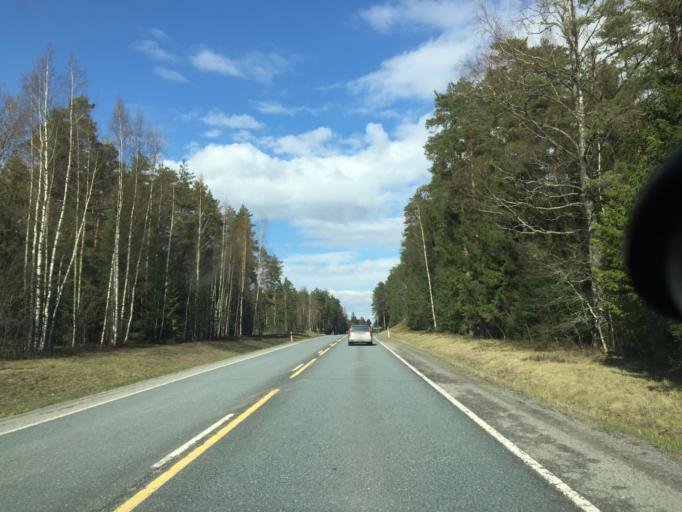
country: FI
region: Uusimaa
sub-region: Raaseporin
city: Inga
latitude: 60.1419
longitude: 23.8883
